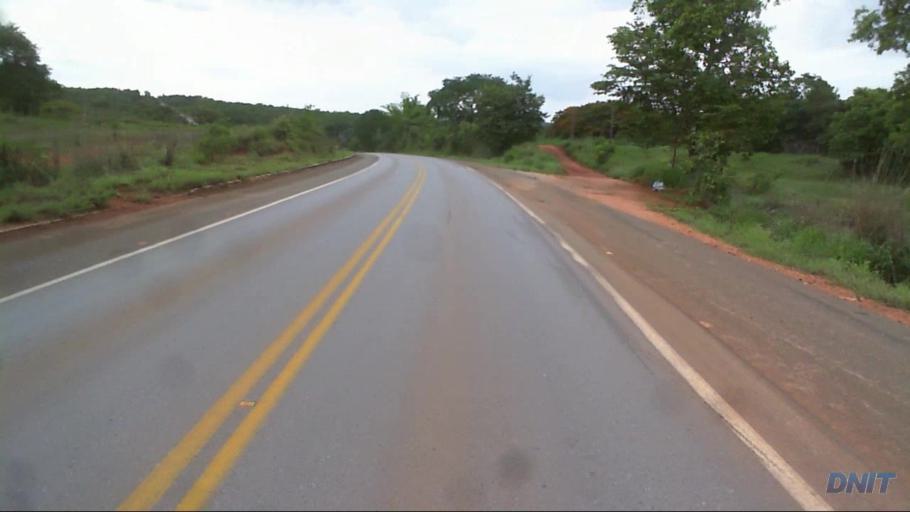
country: BR
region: Goias
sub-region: Uruacu
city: Uruacu
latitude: -14.7505
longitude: -49.0736
